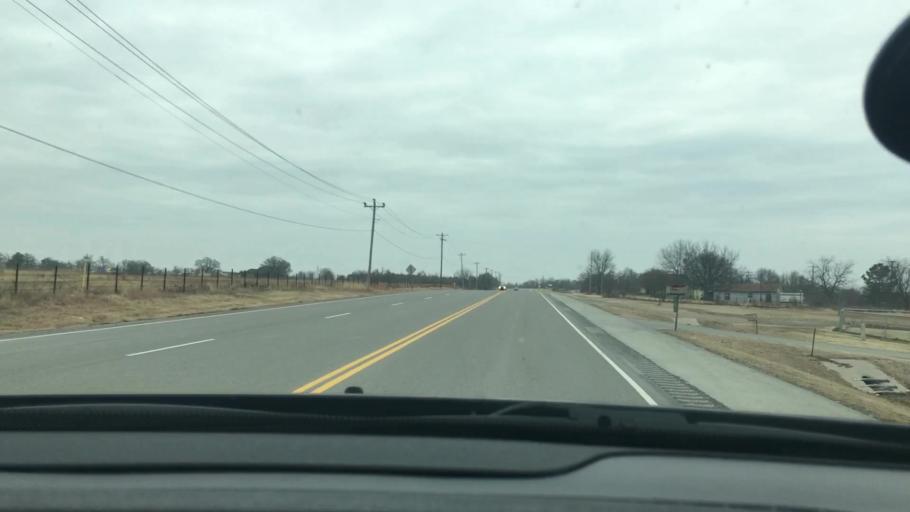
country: US
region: Oklahoma
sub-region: Carter County
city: Healdton
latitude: 34.3979
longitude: -97.5046
